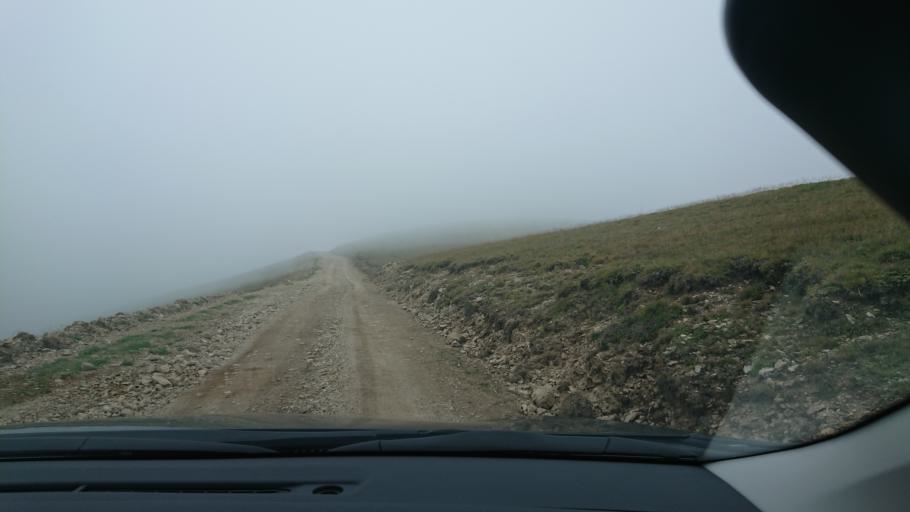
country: TR
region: Gumushane
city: Kurtun
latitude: 40.6239
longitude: 38.9930
